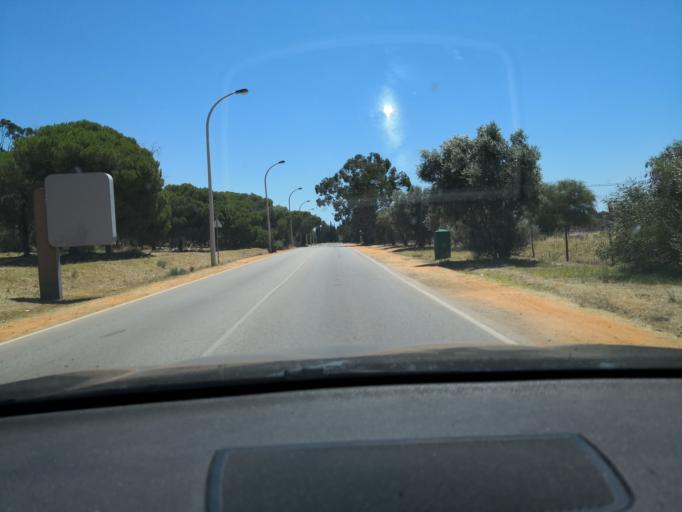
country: PT
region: Faro
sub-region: Loule
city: Boliqueime
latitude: 37.1105
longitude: -8.1418
